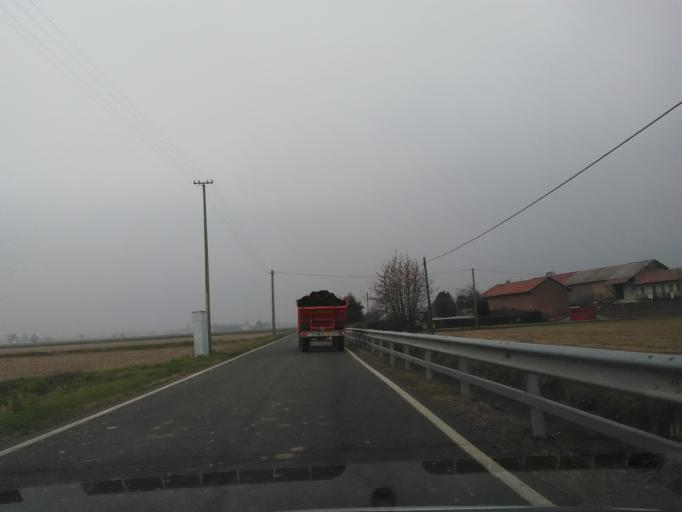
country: IT
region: Piedmont
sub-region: Provincia di Vercelli
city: Crova
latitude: 45.3354
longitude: 8.1989
